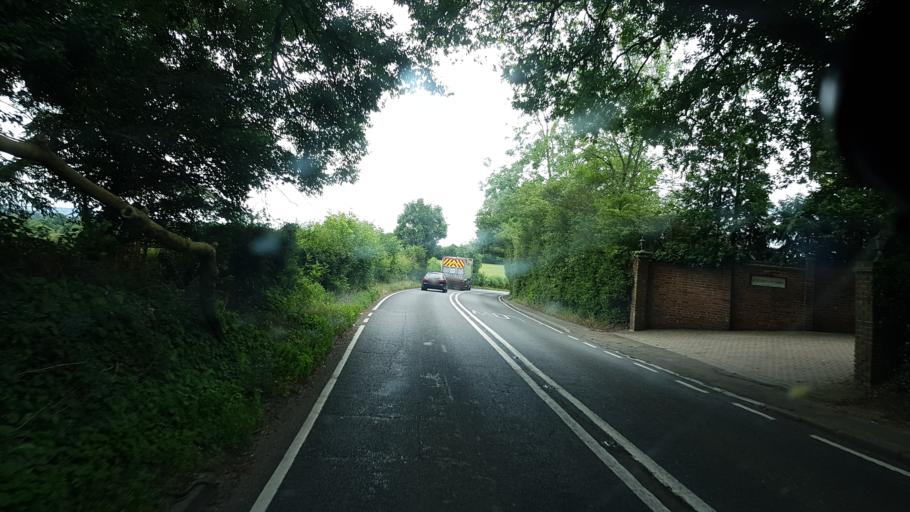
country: GB
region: England
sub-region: Surrey
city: Godstone
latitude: 51.2258
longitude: -0.0470
